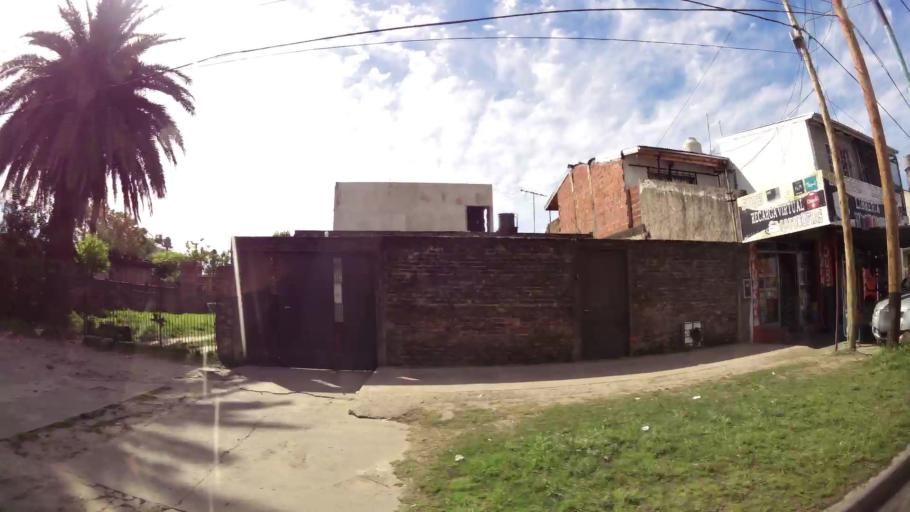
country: AR
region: Buenos Aires
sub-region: Partido de Quilmes
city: Quilmes
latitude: -34.7768
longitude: -58.2970
